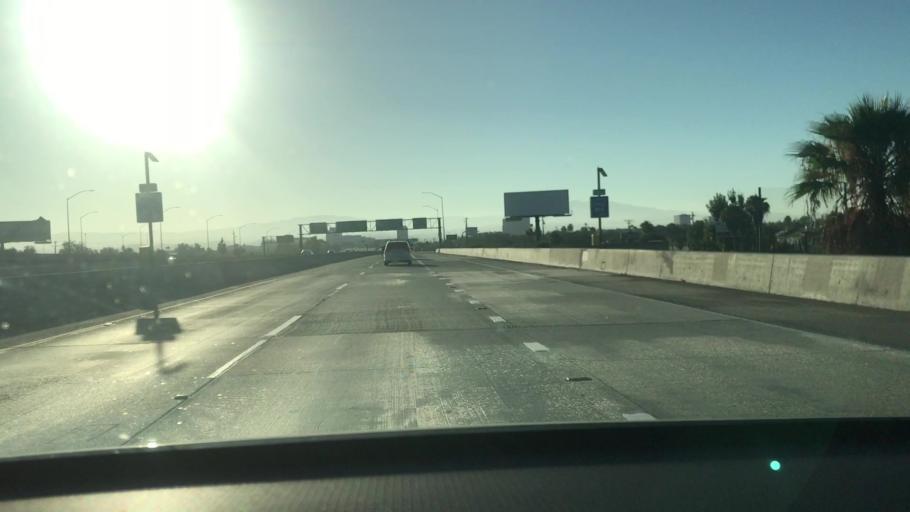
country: US
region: California
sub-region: Orange County
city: Orange
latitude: 33.7788
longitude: -117.8877
